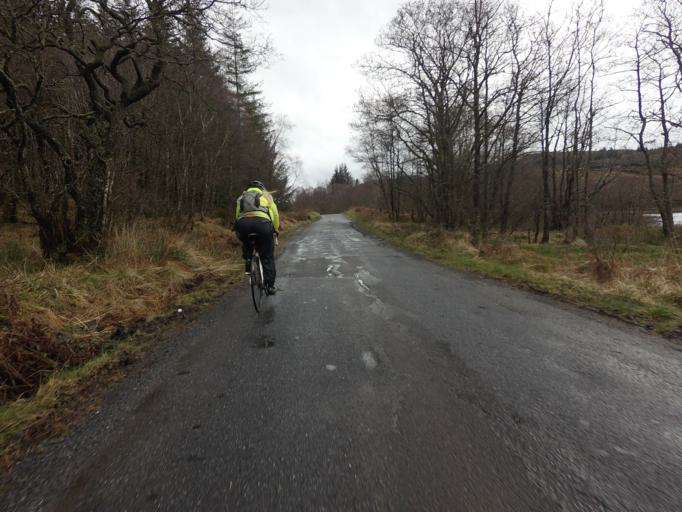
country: GB
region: Scotland
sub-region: West Dunbartonshire
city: Balloch
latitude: 56.2012
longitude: -4.5284
